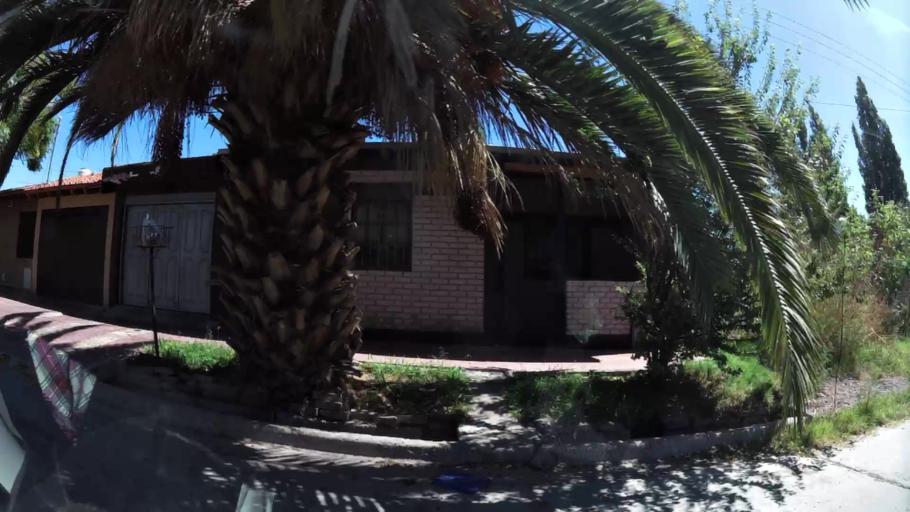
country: AR
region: Mendoza
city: Las Heras
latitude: -32.8589
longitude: -68.8466
